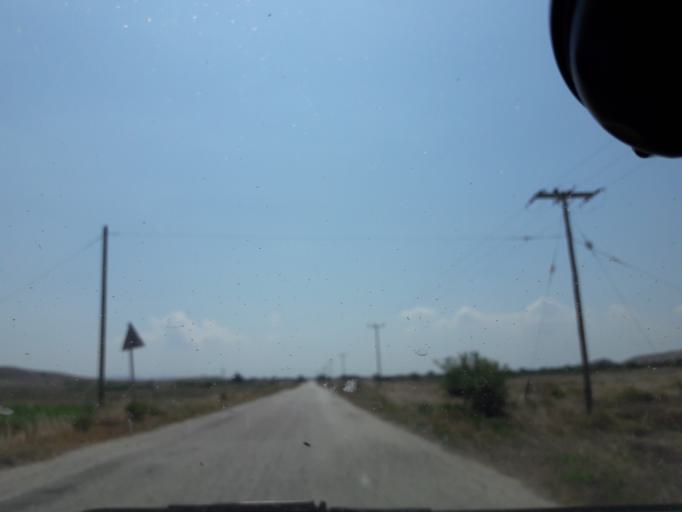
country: GR
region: North Aegean
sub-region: Nomos Lesvou
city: Myrina
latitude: 39.9061
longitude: 25.3071
